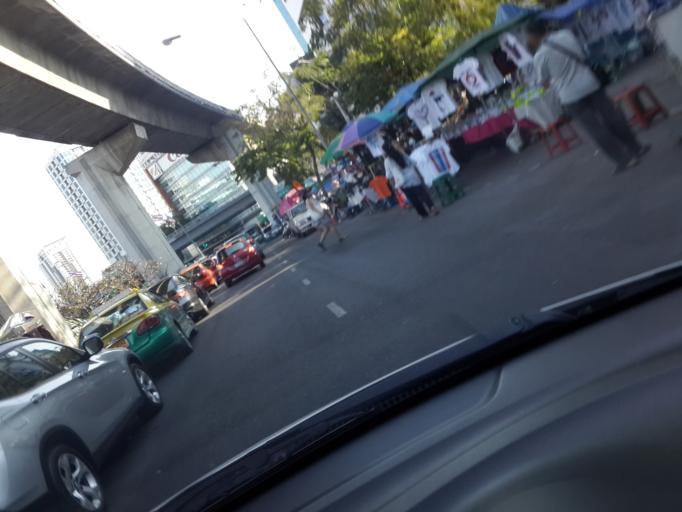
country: TH
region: Bangkok
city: Bang Rak
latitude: 13.7307
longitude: 100.5370
